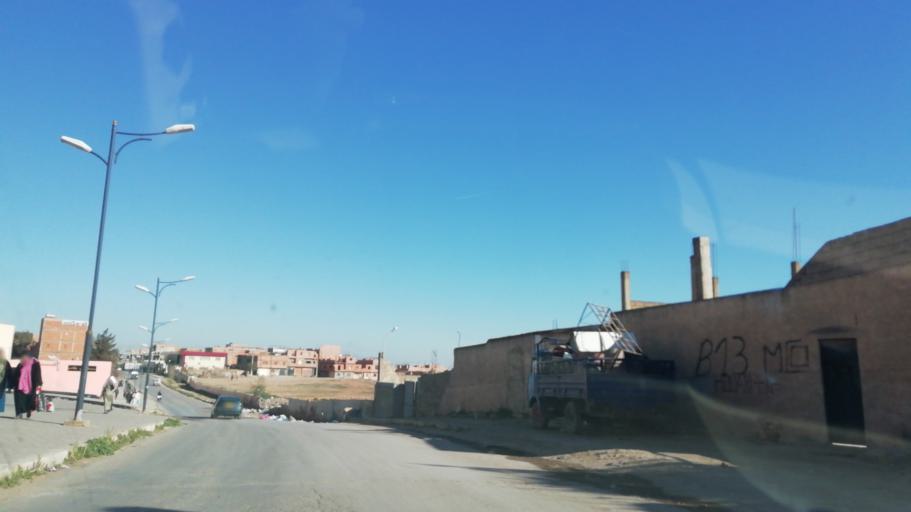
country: DZ
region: Oran
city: Bir el Djir
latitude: 35.7242
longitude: -0.5337
